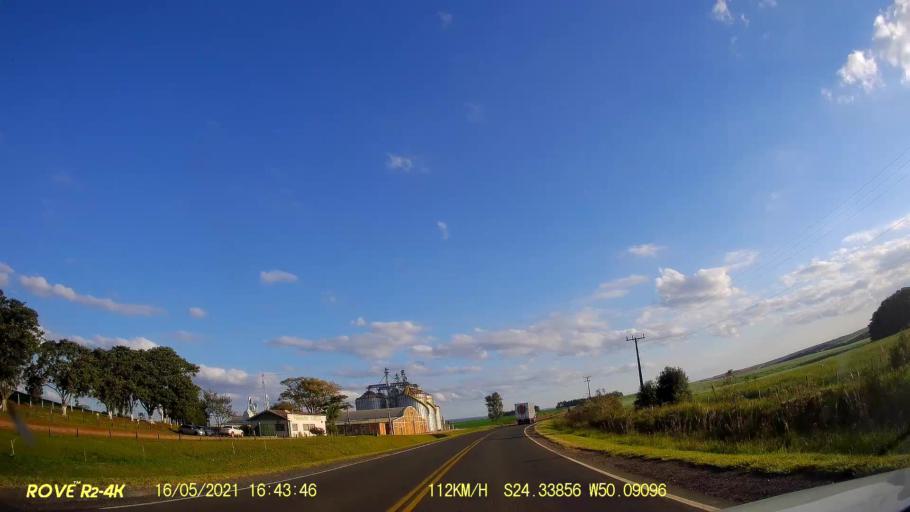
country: BR
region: Parana
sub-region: Pirai Do Sul
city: Pirai do Sul
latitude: -24.3388
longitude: -50.0911
